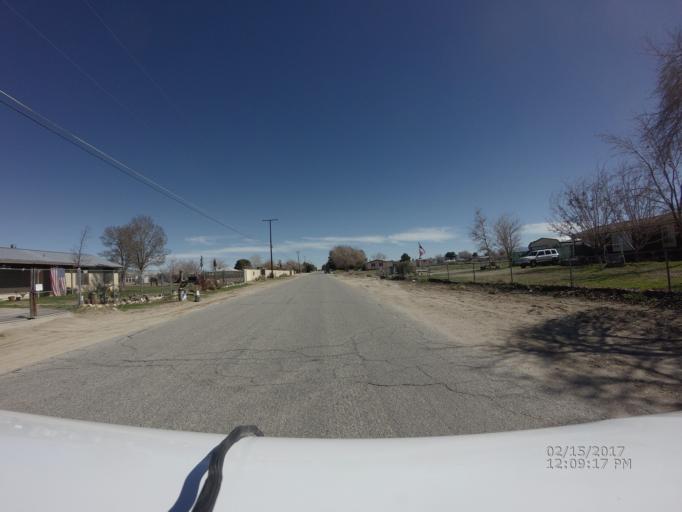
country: US
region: California
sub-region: Los Angeles County
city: Littlerock
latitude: 34.5760
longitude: -117.9596
